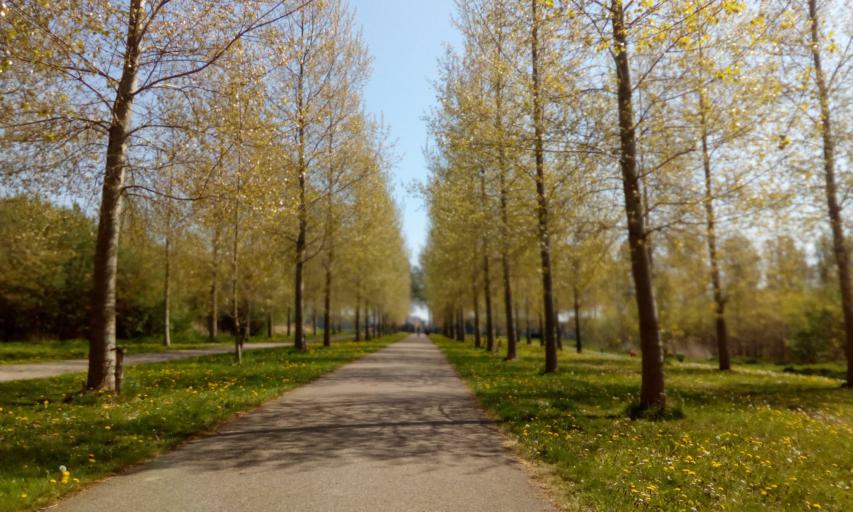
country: NL
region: South Holland
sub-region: Gemeente Hillegom
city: Hillegom
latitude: 52.2571
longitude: 4.6196
